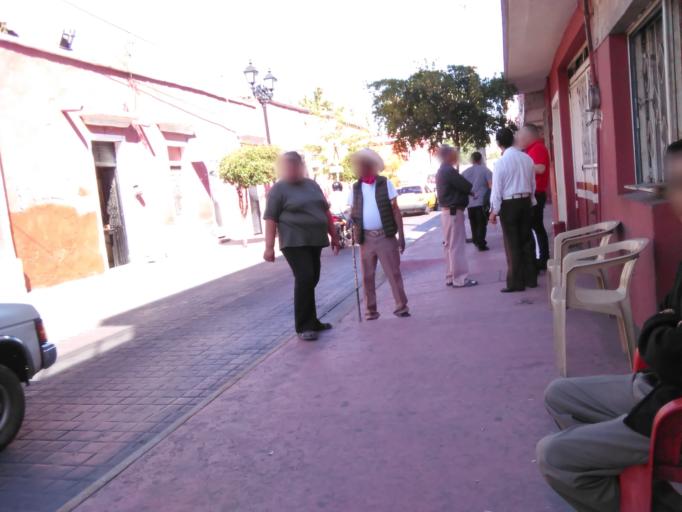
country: MX
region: Nayarit
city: Tepic
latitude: 21.5131
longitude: -104.8902
